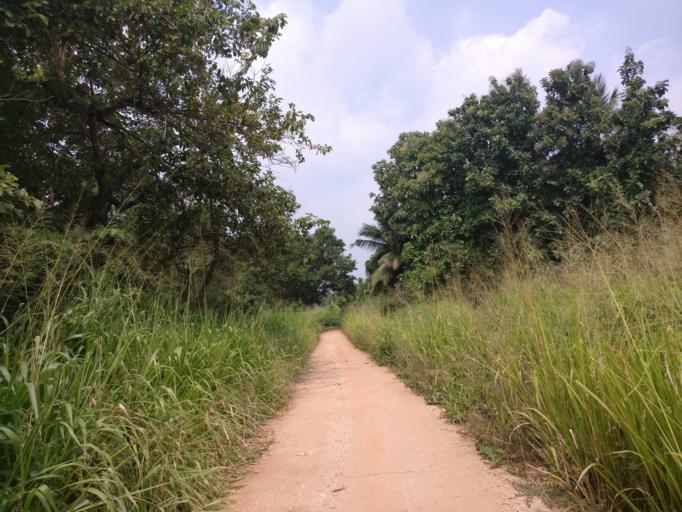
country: LK
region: Central
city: Dambulla
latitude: 7.8381
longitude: 80.6523
